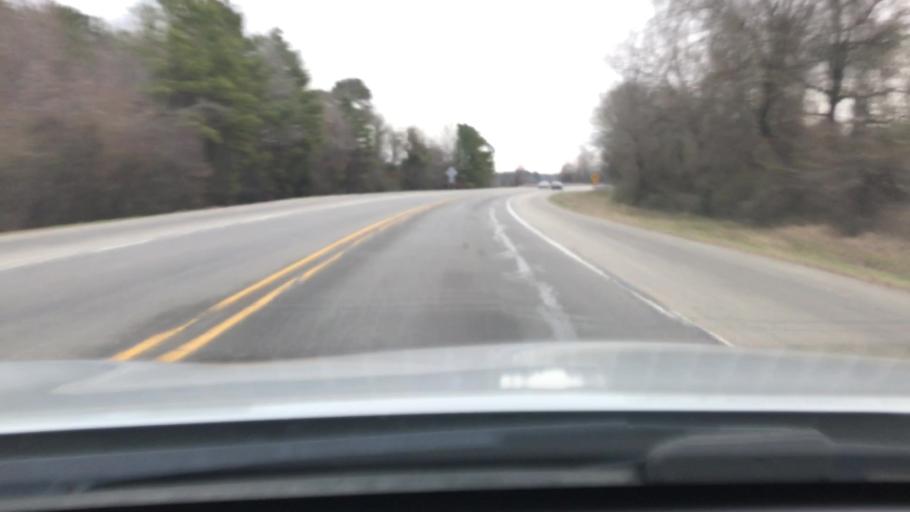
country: US
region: Arkansas
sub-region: Hempstead County
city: Hope
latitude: 33.6878
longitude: -93.5829
